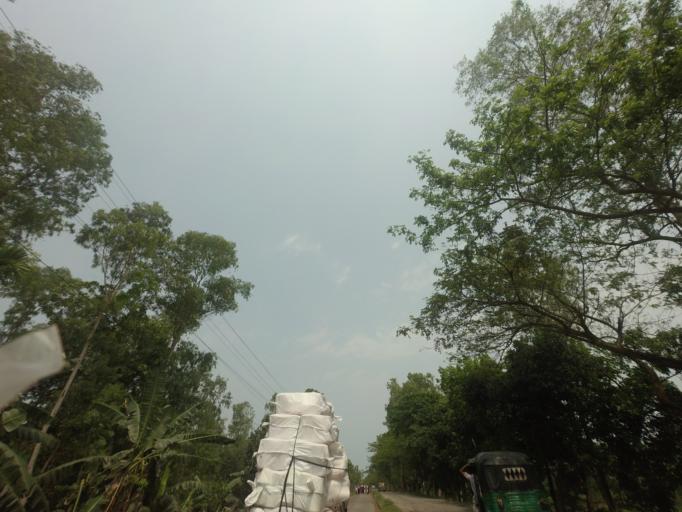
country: BD
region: Rajshahi
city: Sirajganj
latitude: 24.3328
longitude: 89.7003
